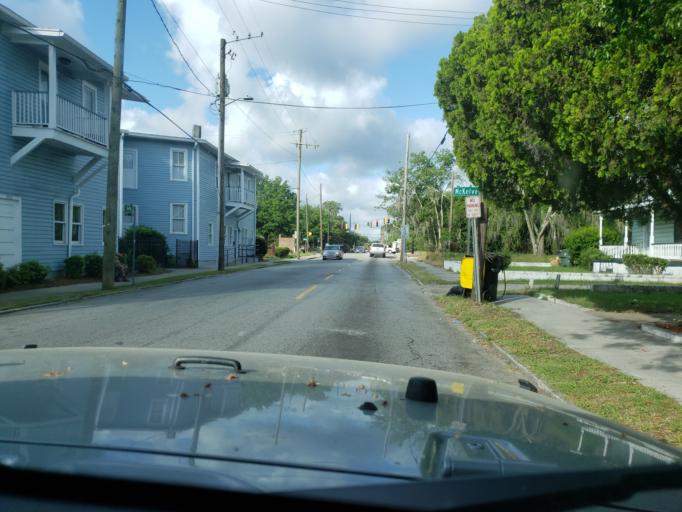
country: US
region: Georgia
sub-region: Chatham County
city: Savannah
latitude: 32.0615
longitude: -81.1100
